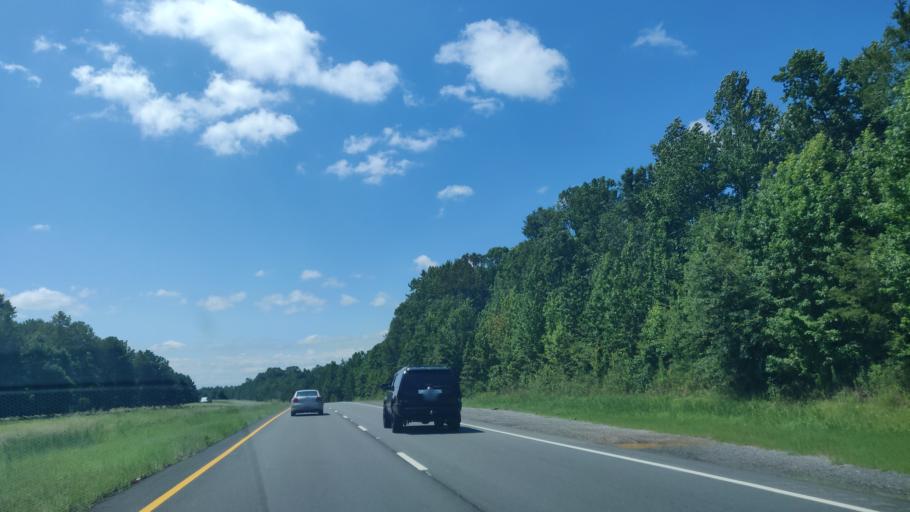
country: US
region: Georgia
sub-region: Chattahoochee County
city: Cusseta
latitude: 32.2234
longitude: -84.7114
